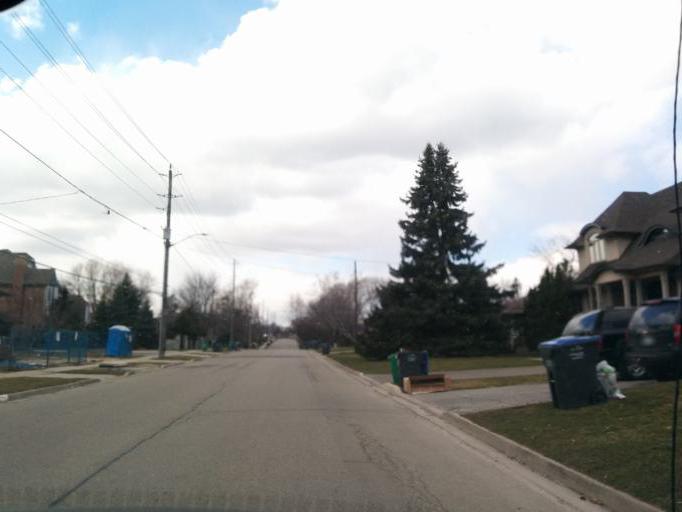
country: CA
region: Ontario
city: Etobicoke
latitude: 43.5896
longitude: -79.5691
